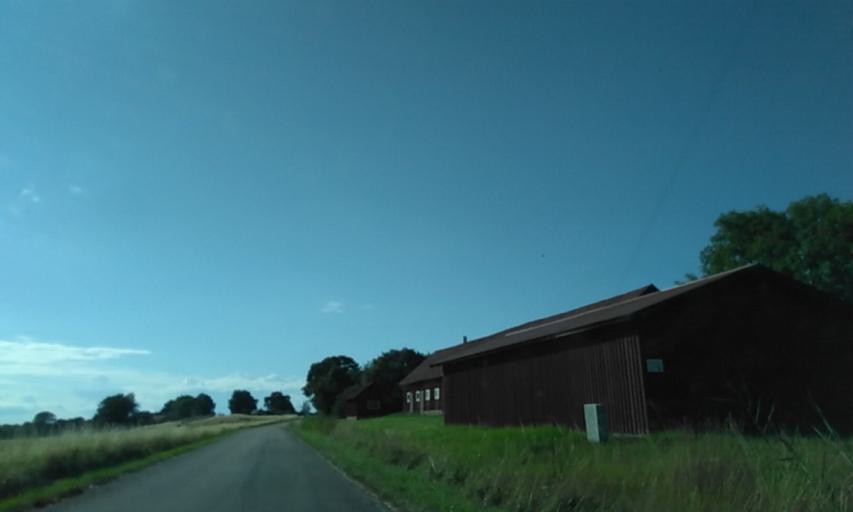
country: SE
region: Vaestra Goetaland
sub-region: Lidkopings Kommun
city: Lidkoping
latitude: 58.5723
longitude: 13.0326
